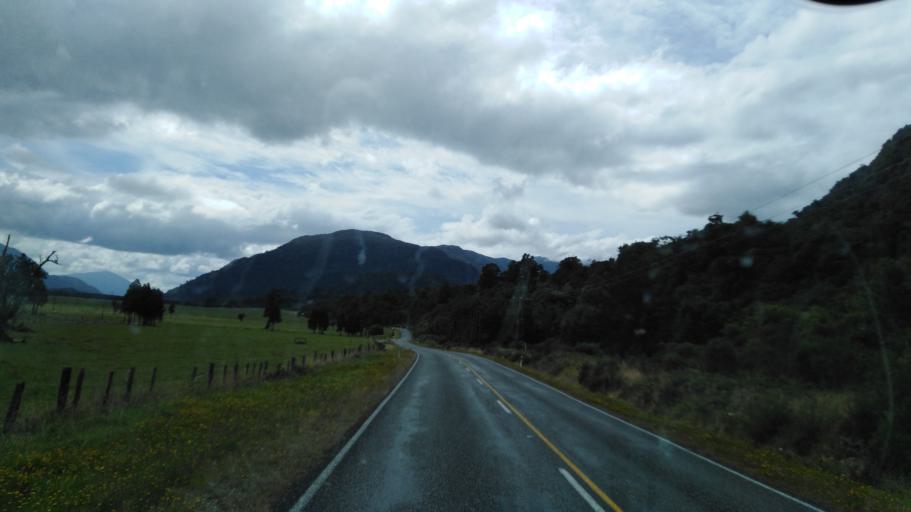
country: NZ
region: West Coast
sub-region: Grey District
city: Greymouth
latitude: -42.7616
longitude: 171.3837
